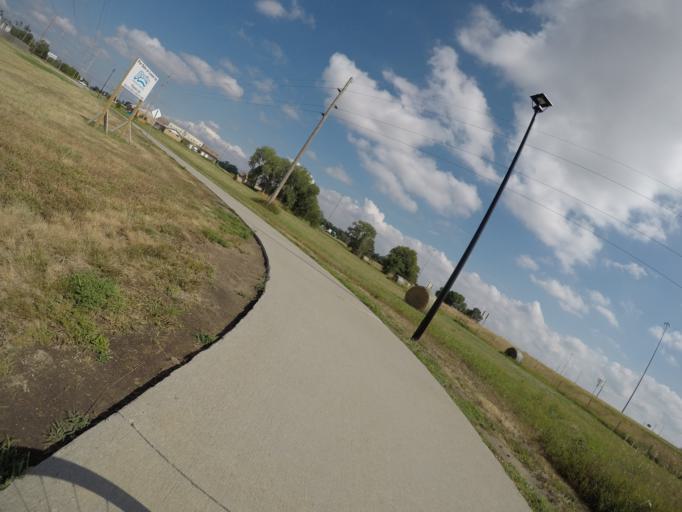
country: US
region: Nebraska
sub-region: Buffalo County
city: Kearney
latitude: 40.6711
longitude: -99.0844
